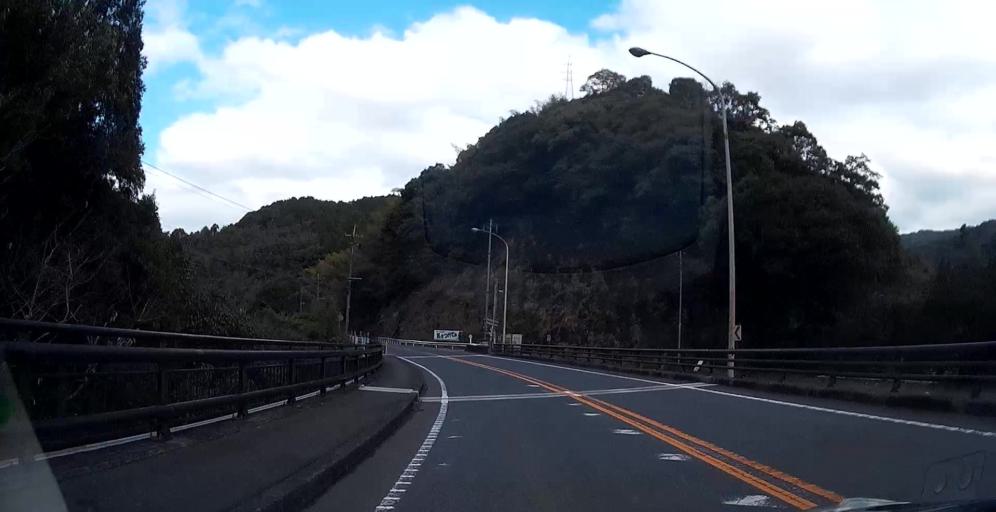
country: JP
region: Kumamoto
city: Yatsushiro
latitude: 32.3752
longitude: 130.5363
